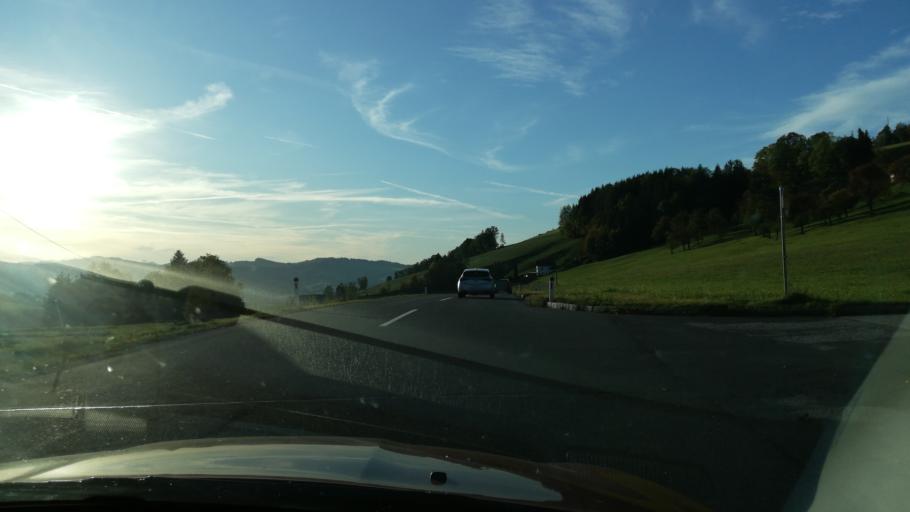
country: AT
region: Upper Austria
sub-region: Politischer Bezirk Kirchdorf an der Krems
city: Gruenburg
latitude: 47.9636
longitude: 14.2999
